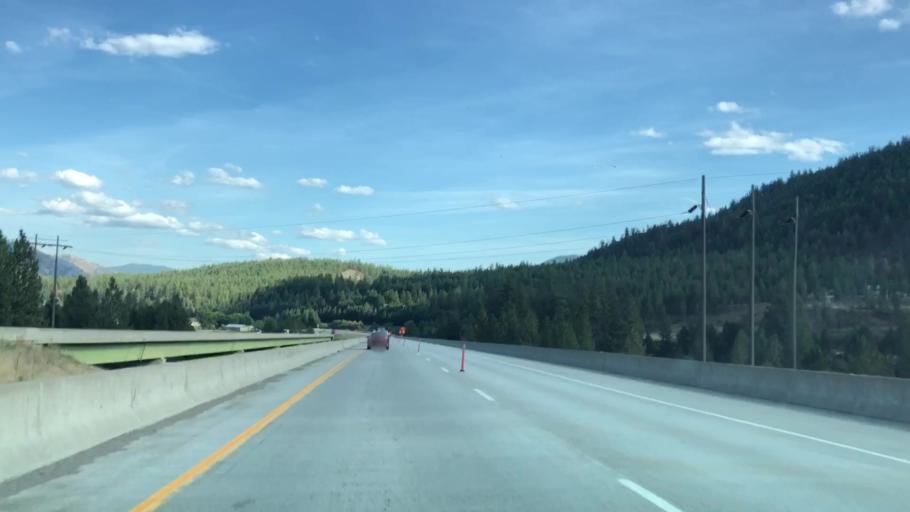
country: US
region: Montana
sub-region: Mineral County
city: Superior
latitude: 47.2342
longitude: -115.0210
